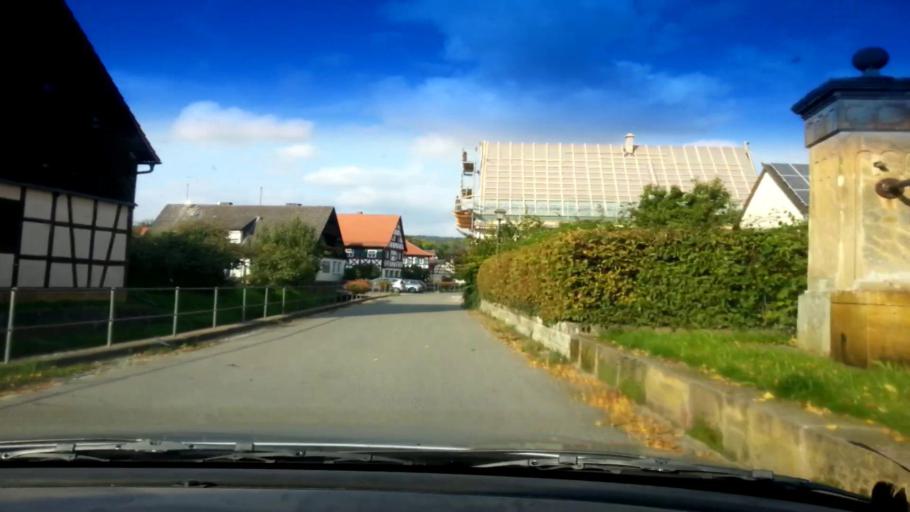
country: DE
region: Bavaria
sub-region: Upper Franconia
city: Schesslitz
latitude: 49.9889
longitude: 11.0457
